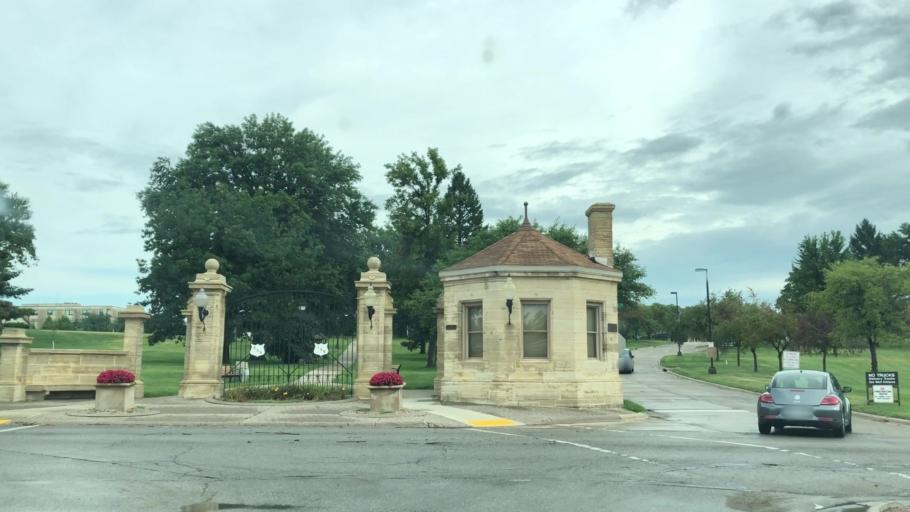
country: US
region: Iowa
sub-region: Marshall County
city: Marshalltown
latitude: 42.0526
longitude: -92.9347
